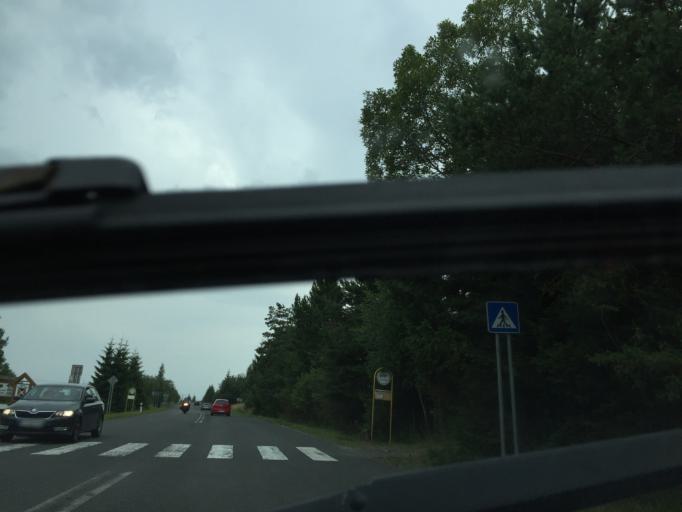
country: SK
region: Presovsky
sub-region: Okres Poprad
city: Vysoke Tatry
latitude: 49.1305
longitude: 20.1988
